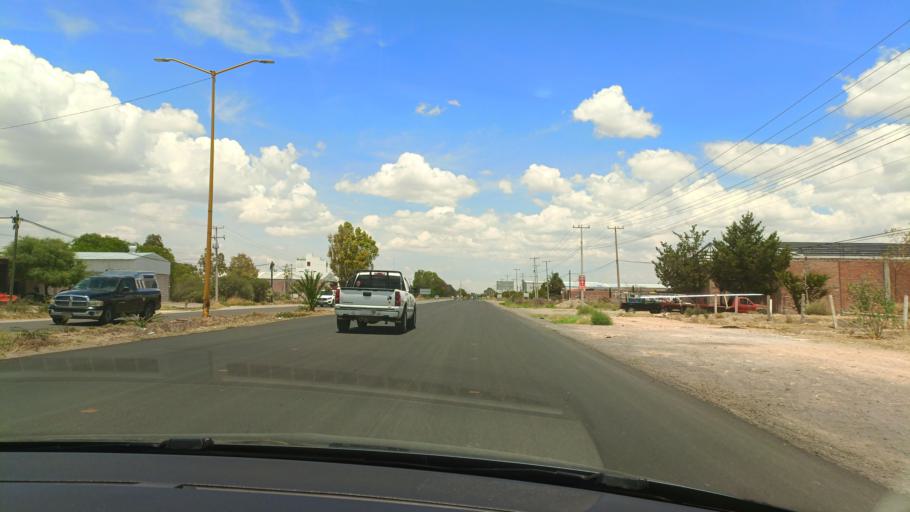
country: MX
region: Guanajuato
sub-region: San Luis de la Paz
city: San Ignacio
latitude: 21.2874
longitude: -100.5594
